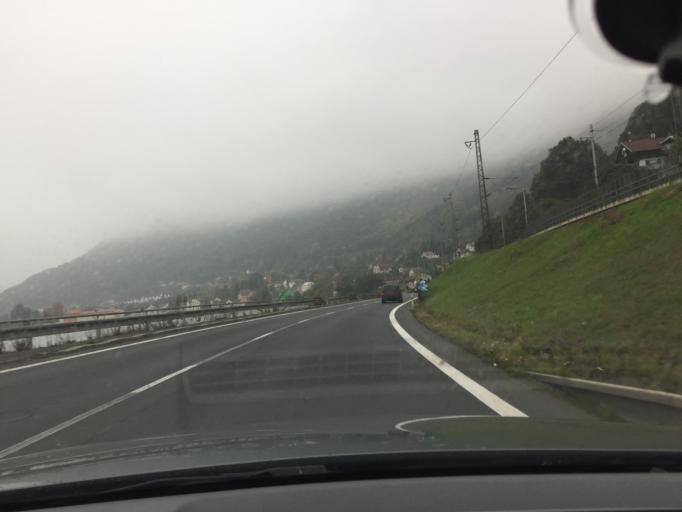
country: CZ
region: Ustecky
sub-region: Okres Usti nad Labem
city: Usti nad Labem
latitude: 50.6299
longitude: 14.0505
